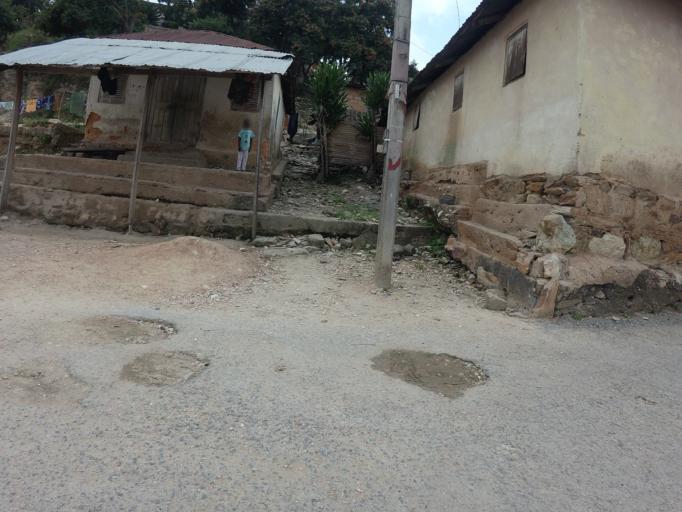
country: TG
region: Plateaux
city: Kpalime
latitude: 6.8889
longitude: 0.4572
